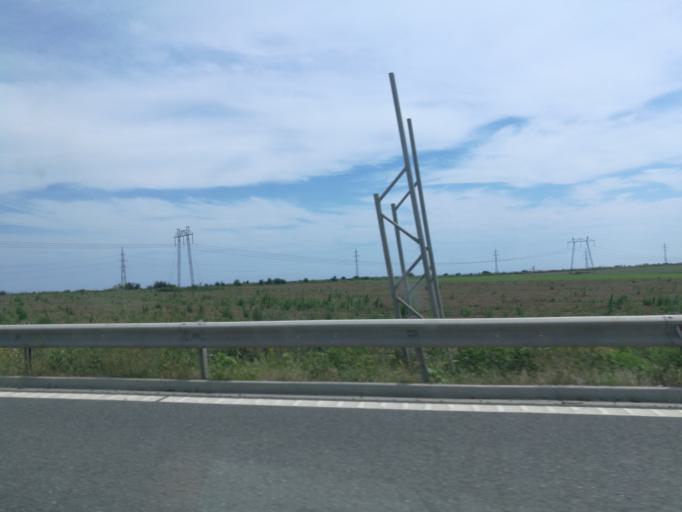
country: RO
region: Constanta
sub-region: Comuna Ovidiu
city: Ovidiu
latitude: 44.2230
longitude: 28.5513
